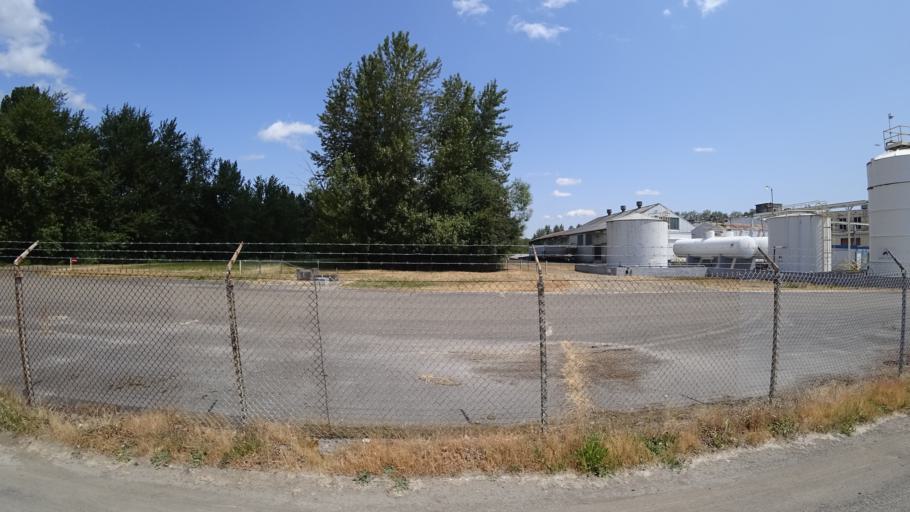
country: US
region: Washington
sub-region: Clark County
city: Vancouver
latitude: 45.6158
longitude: -122.7140
